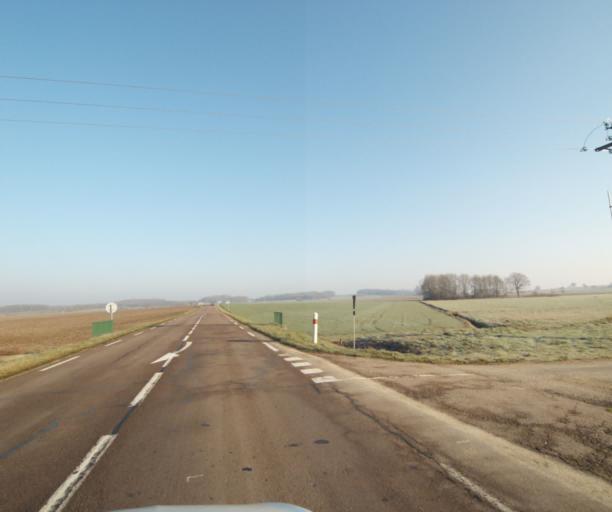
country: FR
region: Champagne-Ardenne
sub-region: Departement de la Haute-Marne
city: Montier-en-Der
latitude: 48.4375
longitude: 4.7292
